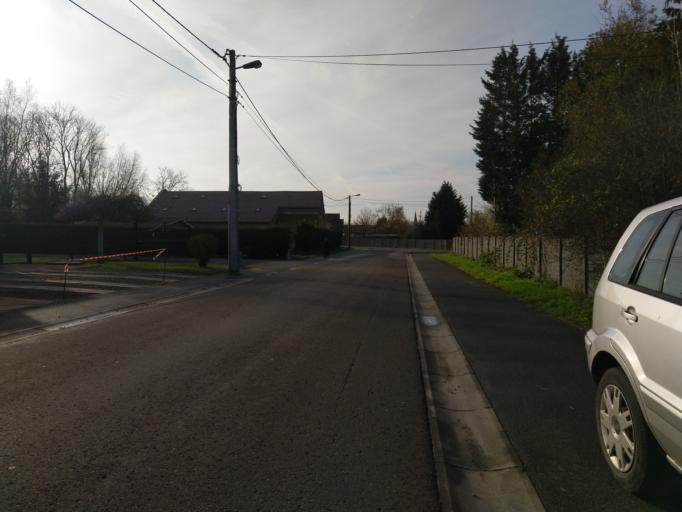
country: BE
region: Wallonia
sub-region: Province du Hainaut
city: Hensies
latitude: 50.4409
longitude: 3.6850
